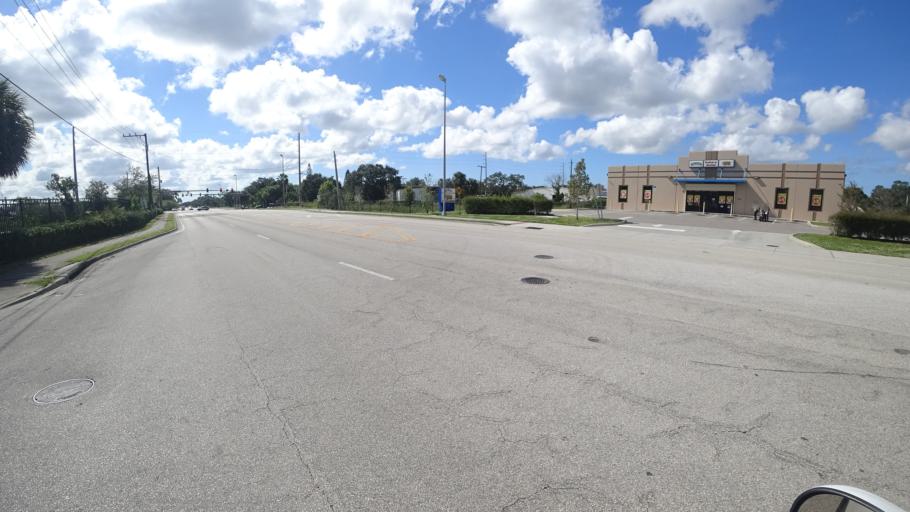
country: US
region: Florida
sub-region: Manatee County
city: Bradenton
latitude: 27.4930
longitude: -82.5547
